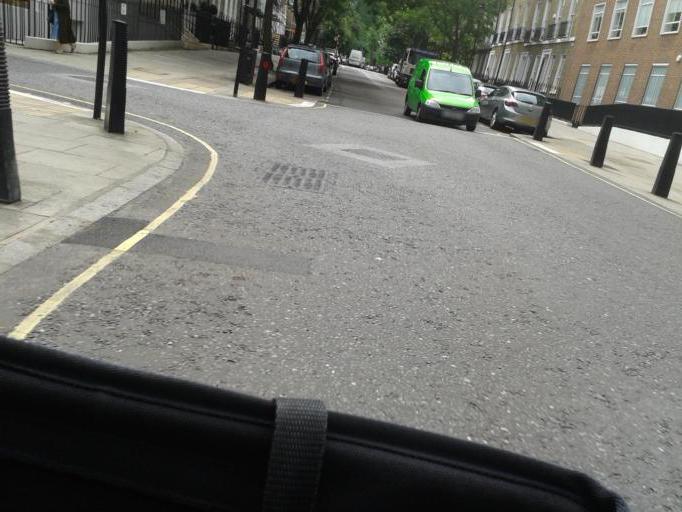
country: GB
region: England
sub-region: Greater London
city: Clerkenwell
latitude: 51.5231
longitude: -0.1159
